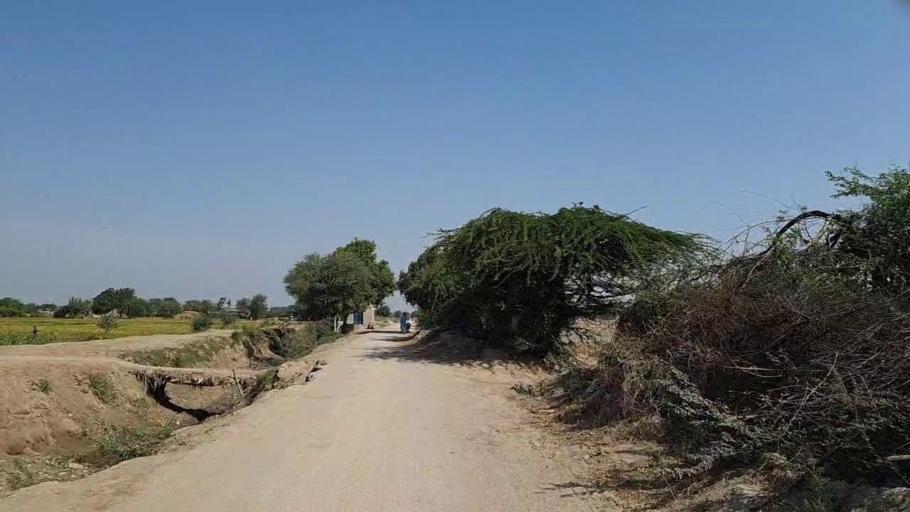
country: PK
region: Sindh
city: Mirpur Batoro
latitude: 24.6814
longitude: 68.2579
